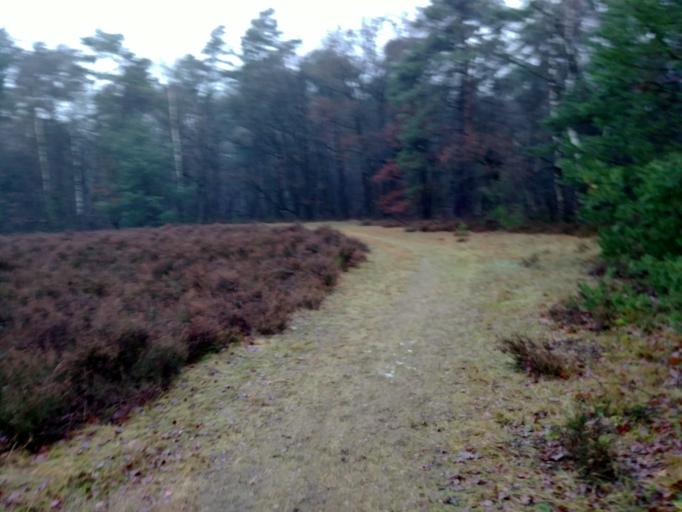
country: NL
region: Gelderland
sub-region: Gemeente Barneveld
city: Garderen
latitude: 52.2234
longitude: 5.7020
